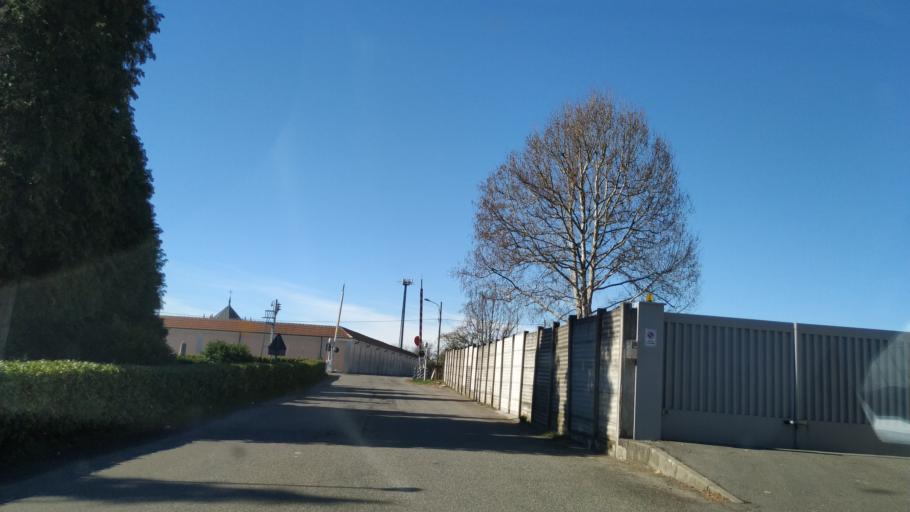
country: IT
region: Piedmont
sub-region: Provincia di Novara
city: Ghemme
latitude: 45.5928
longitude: 8.4223
